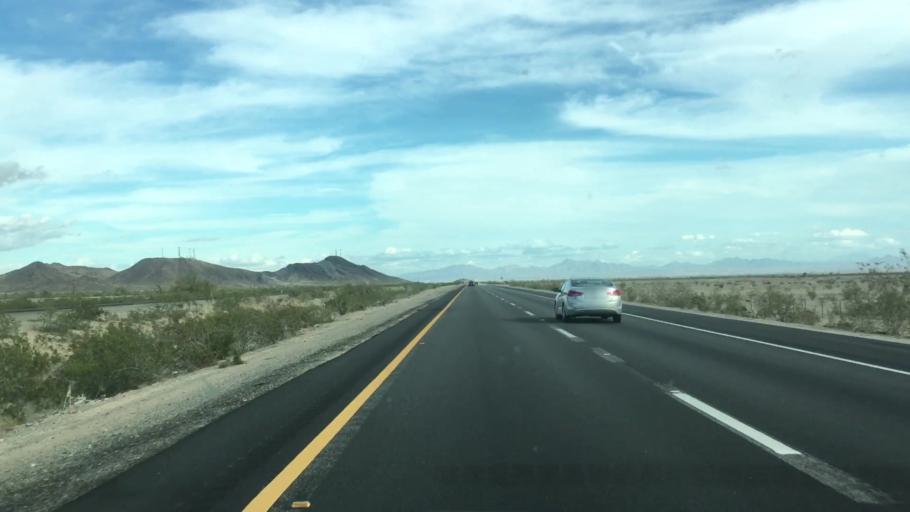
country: US
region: California
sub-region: Riverside County
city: Mesa Verde
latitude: 33.6097
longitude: -114.8026
